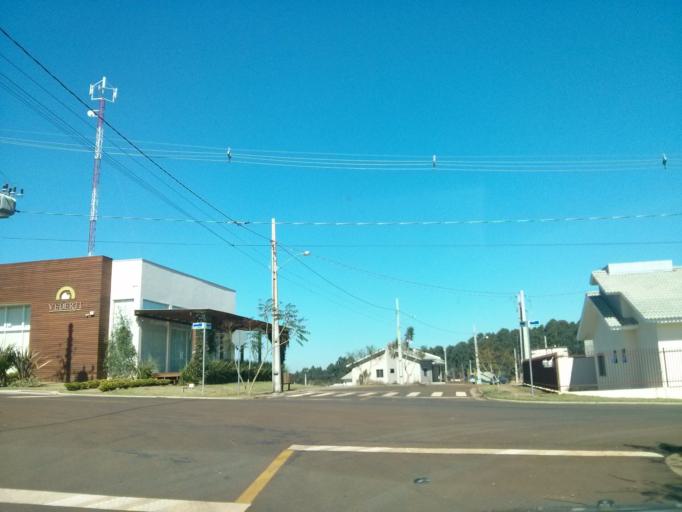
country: BR
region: Santa Catarina
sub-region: Chapeco
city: Chapeco
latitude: -27.0895
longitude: -52.7127
